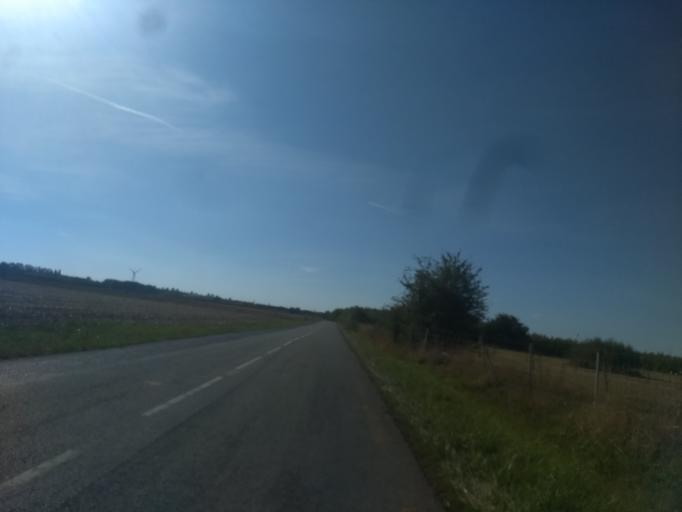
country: FR
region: Nord-Pas-de-Calais
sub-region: Departement du Pas-de-Calais
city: Roeux
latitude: 50.2733
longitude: 2.8823
